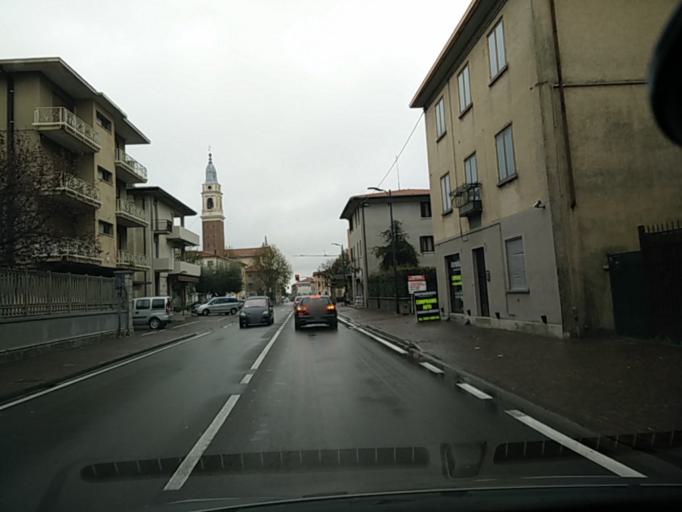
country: IT
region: Veneto
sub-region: Provincia di Vicenza
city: Rosa
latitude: 45.7260
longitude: 11.7623
